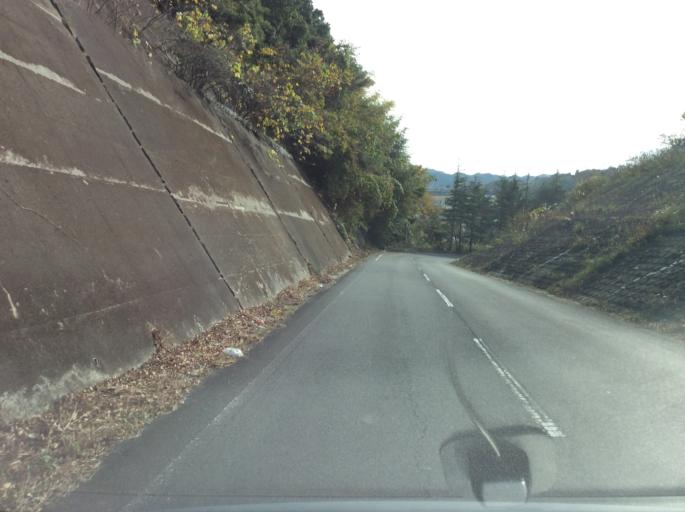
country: JP
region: Fukushima
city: Iwaki
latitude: 37.0816
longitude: 140.9429
